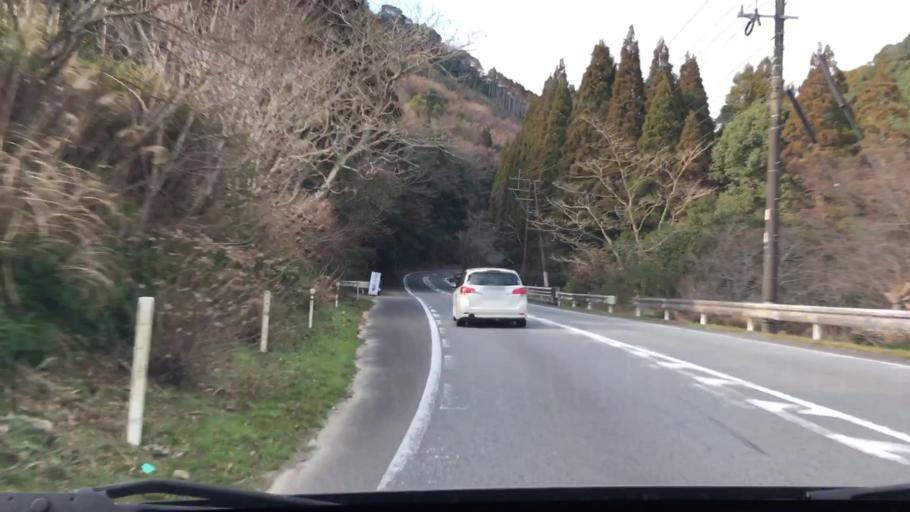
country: JP
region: Miyazaki
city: Nichinan
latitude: 31.7466
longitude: 131.3352
